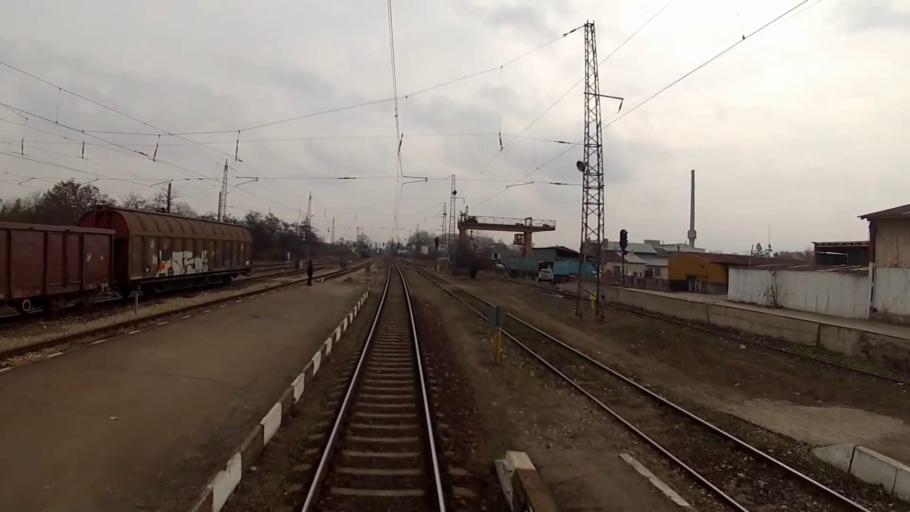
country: BG
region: Sofia-Capital
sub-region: Stolichna Obshtina
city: Sofia
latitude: 42.6577
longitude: 23.4453
